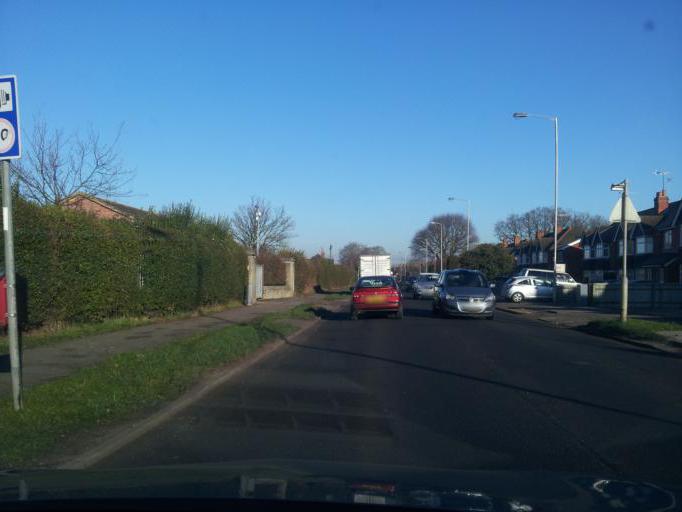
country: GB
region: England
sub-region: West Berkshire
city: Tilehurst
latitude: 51.4512
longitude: -1.0466
